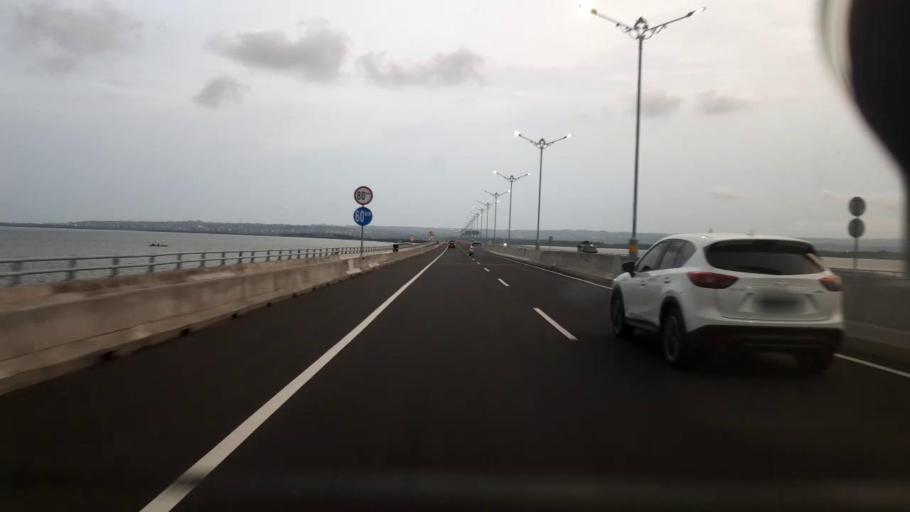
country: ID
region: Bali
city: Kelanabian
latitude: -8.7505
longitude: 115.1956
